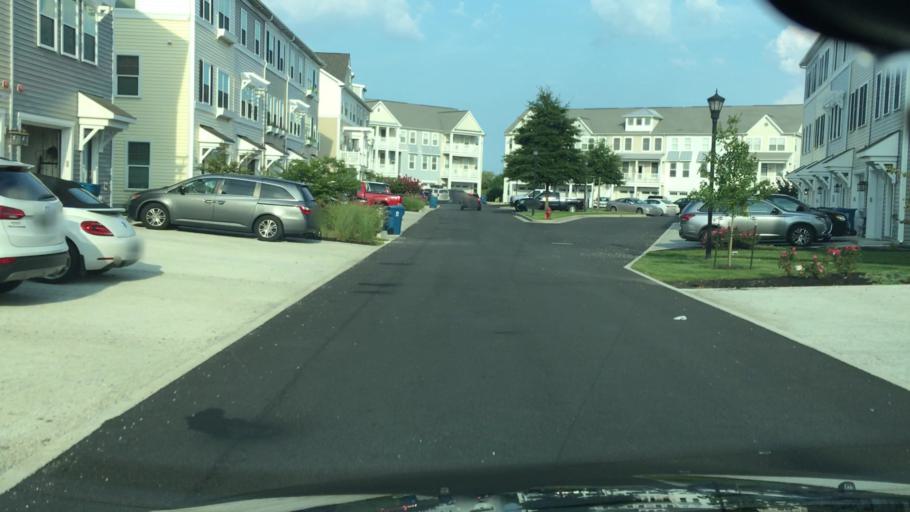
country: US
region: Maryland
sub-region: Worcester County
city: West Ocean City
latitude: 38.3381
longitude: -75.1038
